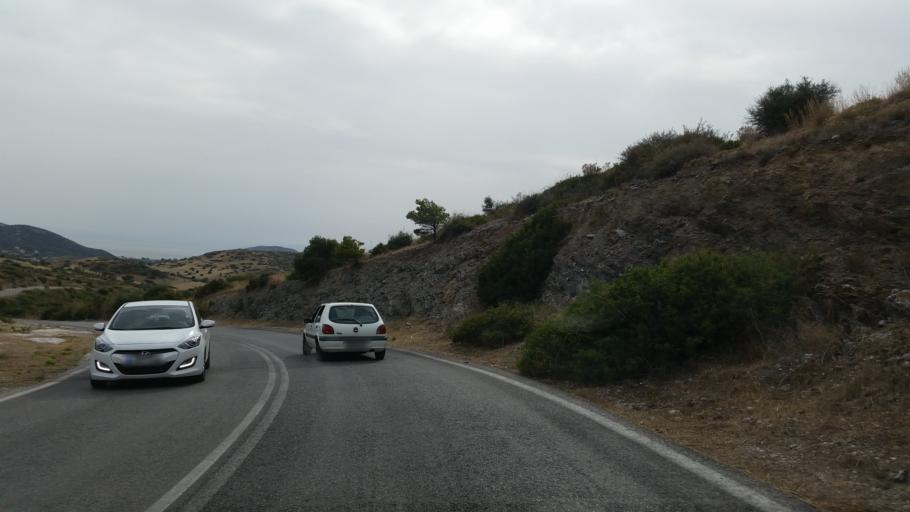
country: GR
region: Attica
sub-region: Nomarchia Anatolikis Attikis
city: Palaia Fokaia
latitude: 37.7301
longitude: 23.9863
